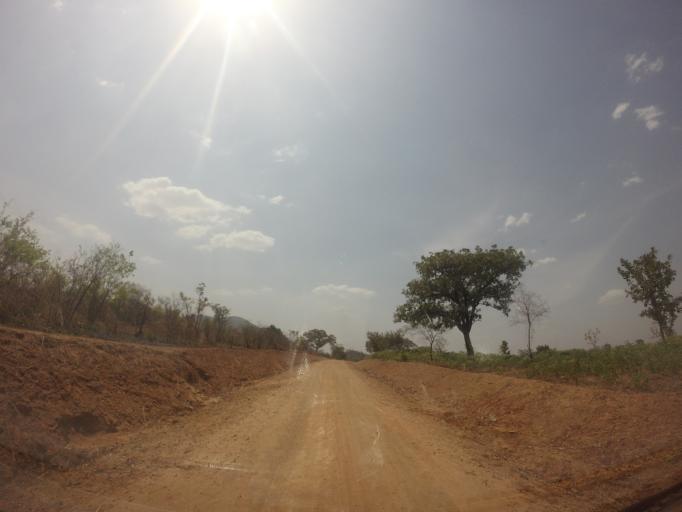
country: UG
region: Northern Region
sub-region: Arua District
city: Arua
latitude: 2.8968
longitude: 31.1154
